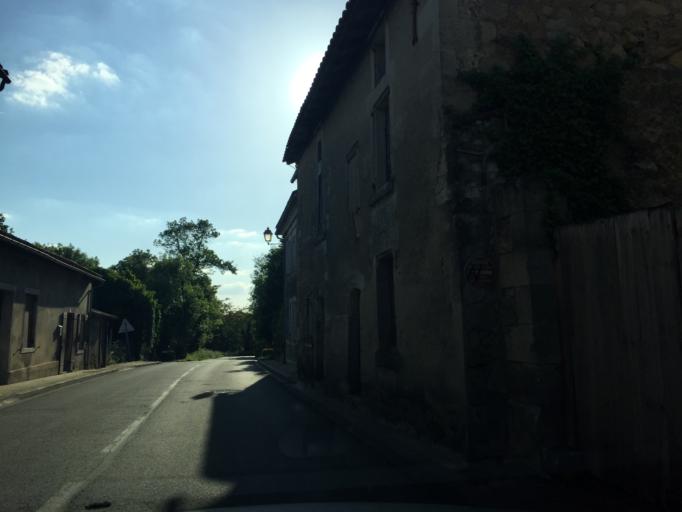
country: FR
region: Aquitaine
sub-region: Departement de la Dordogne
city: La Roche-Chalais
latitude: 45.2051
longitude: 0.0338
